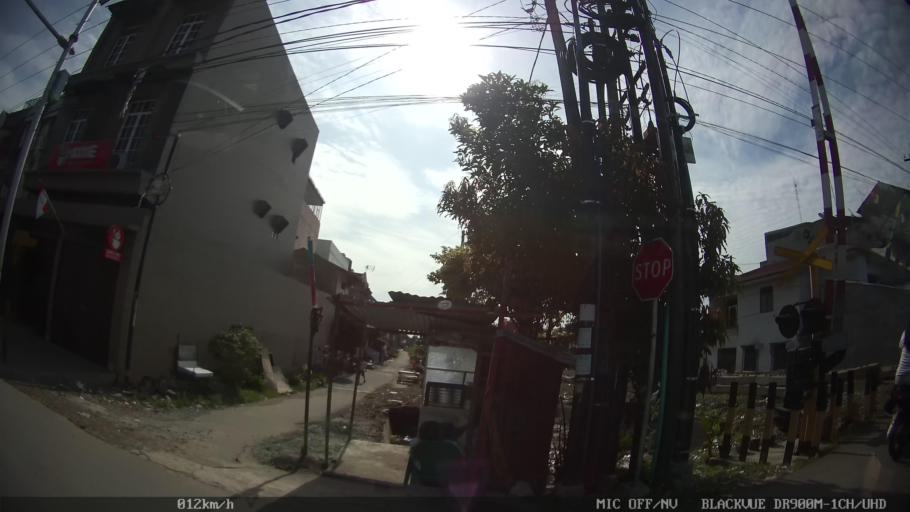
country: ID
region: North Sumatra
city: Medan
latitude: 3.6021
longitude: 98.6453
